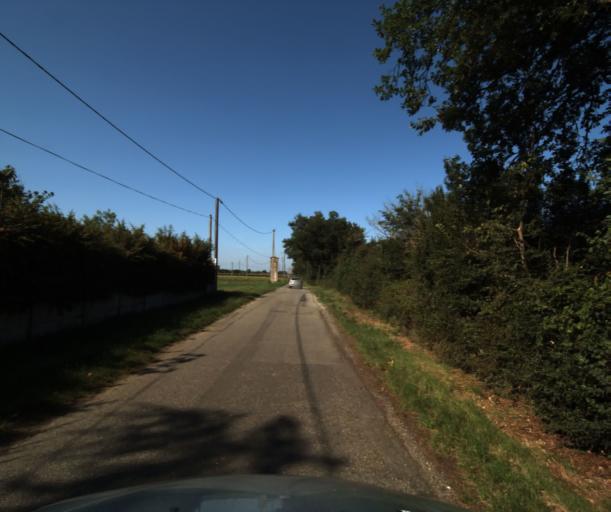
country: FR
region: Midi-Pyrenees
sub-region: Departement de la Haute-Garonne
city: Le Fauga
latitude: 43.4197
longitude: 1.3064
